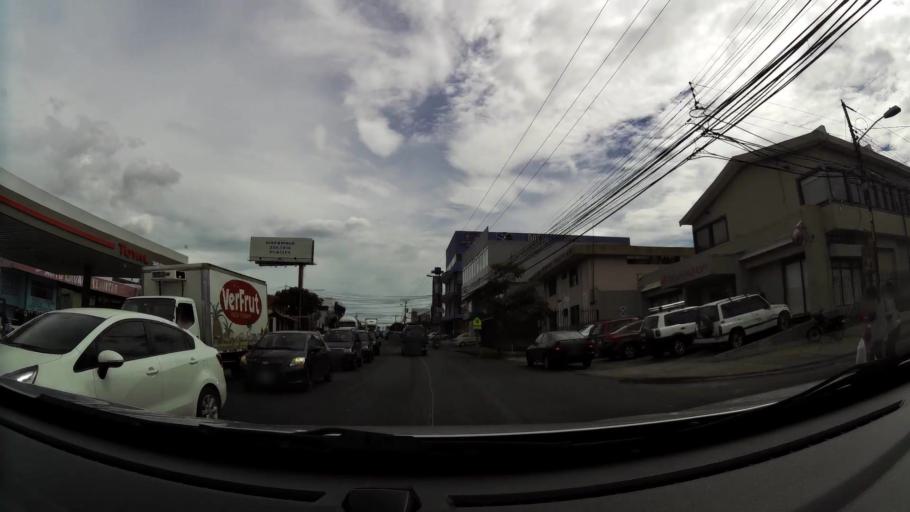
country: CR
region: San Jose
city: San Pedro
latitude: 9.9115
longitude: -84.0600
